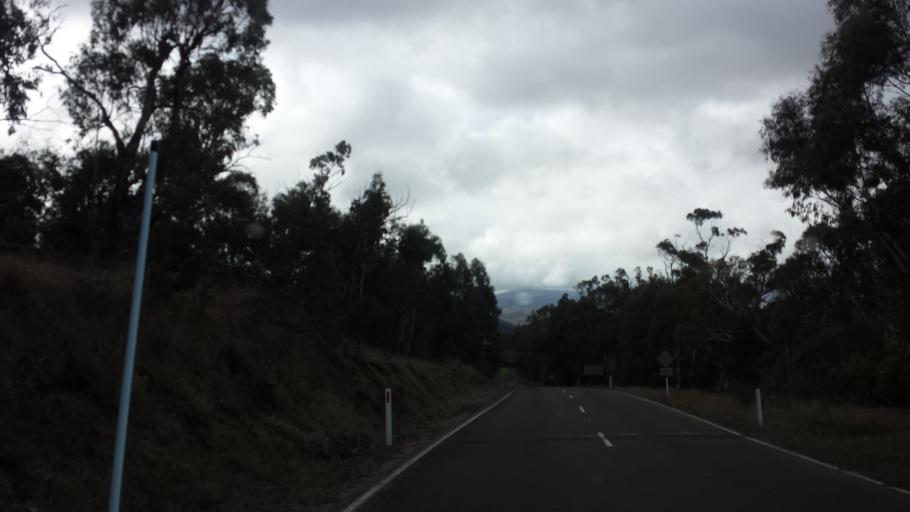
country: AU
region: Victoria
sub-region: Alpine
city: Mount Beauty
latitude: -37.1245
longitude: 147.5382
